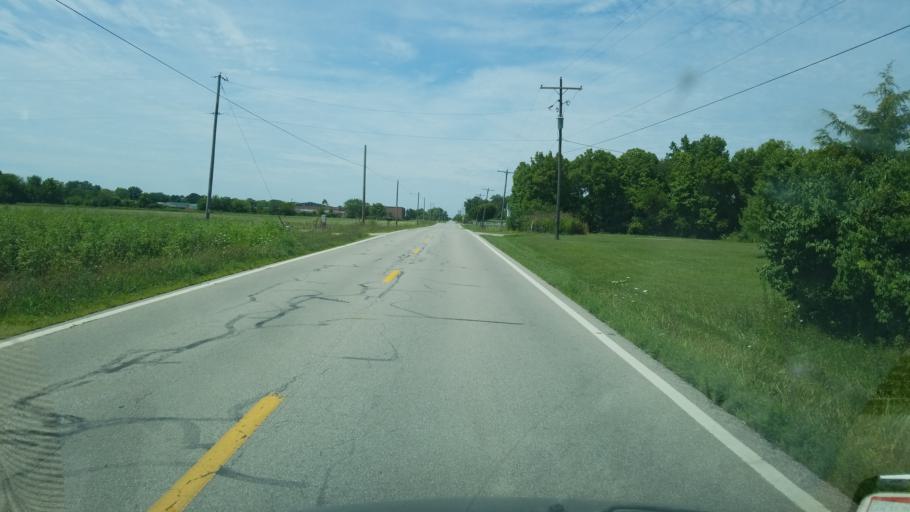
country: US
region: Ohio
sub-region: Franklin County
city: Grove City
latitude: 39.8754
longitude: -83.1785
